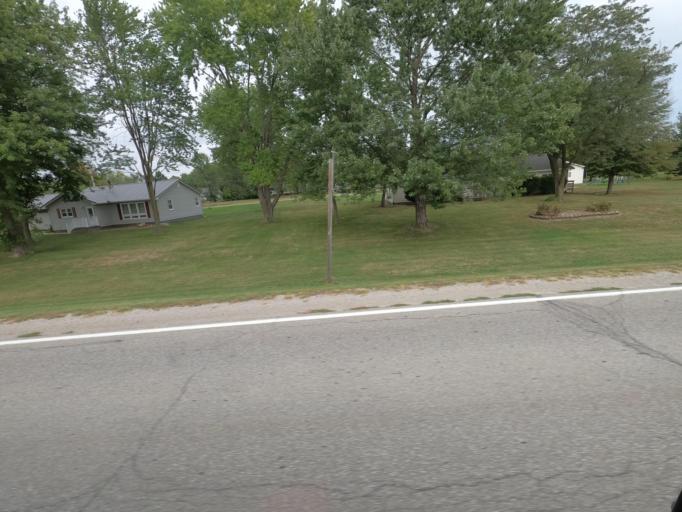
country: US
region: Iowa
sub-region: Wapello County
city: Ottumwa
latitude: 40.9143
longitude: -92.2155
